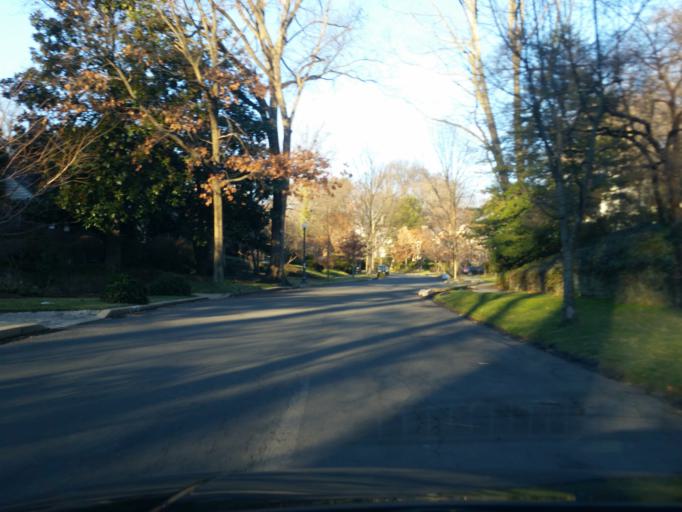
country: US
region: Maryland
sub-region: Montgomery County
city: Brookmont
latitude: 38.9376
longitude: -77.1003
